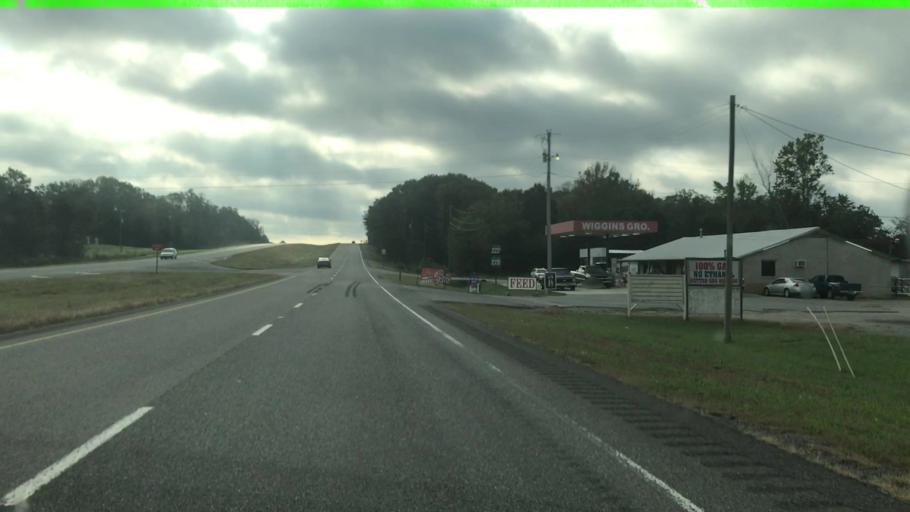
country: US
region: Alabama
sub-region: Morgan County
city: Danville
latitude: 34.4162
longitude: -87.1608
